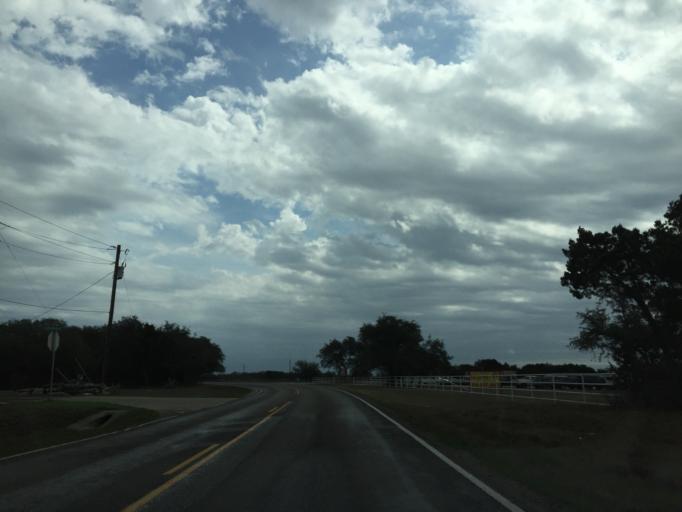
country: US
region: Texas
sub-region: Burnet County
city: Bertram
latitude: 30.6547
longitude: -98.0039
